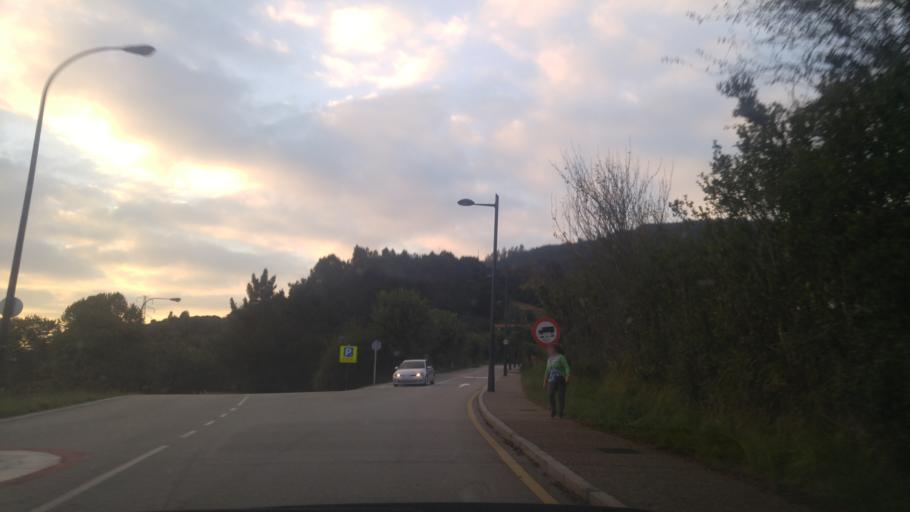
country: ES
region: Asturias
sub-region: Province of Asturias
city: Oviedo
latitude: 43.3763
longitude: -5.8654
